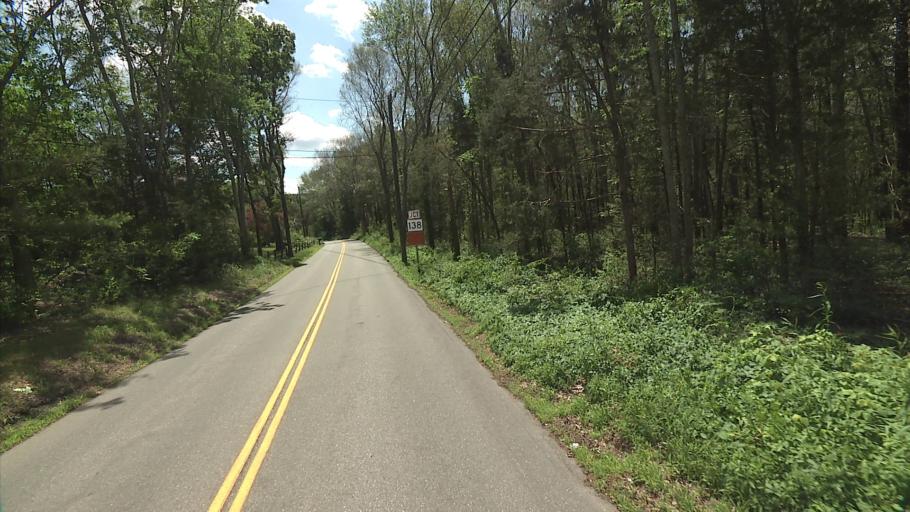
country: US
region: Connecticut
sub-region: New London County
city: Jewett City
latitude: 41.5839
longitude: -71.9010
